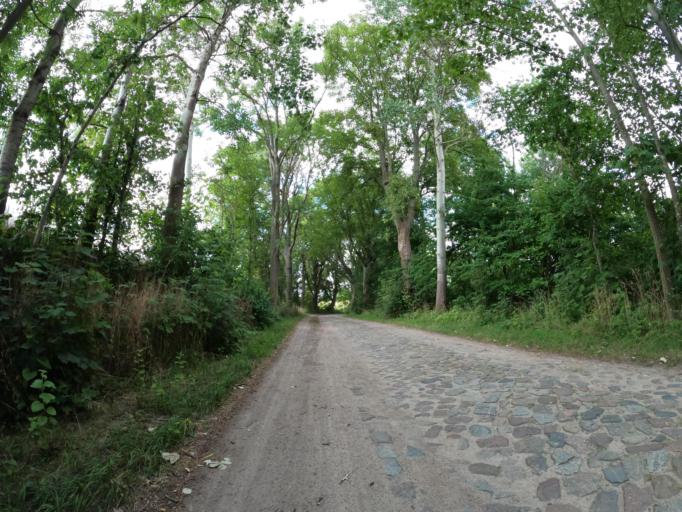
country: DE
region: Mecklenburg-Vorpommern
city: Woldegk
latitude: 53.4067
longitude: 13.6209
